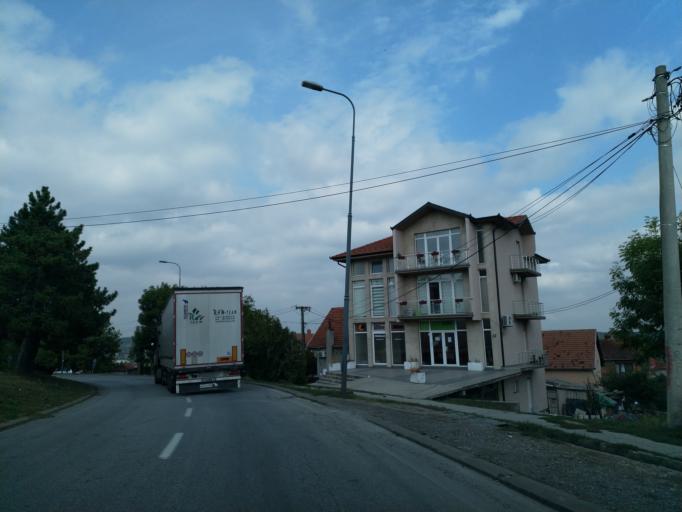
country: RS
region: Central Serbia
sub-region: Sumadijski Okrug
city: Kragujevac
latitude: 44.0312
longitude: 20.9160
